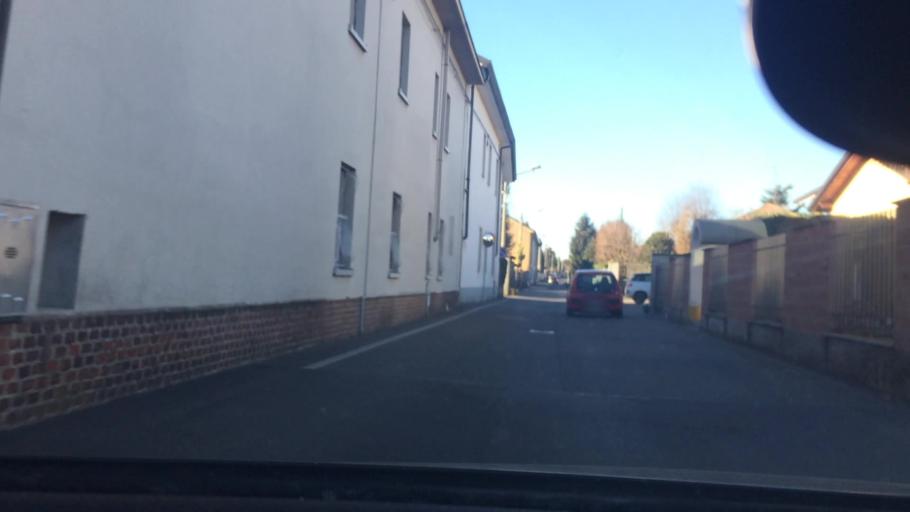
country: IT
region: Lombardy
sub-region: Provincia di Monza e Brianza
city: Ceriano Laghetto
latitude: 45.6263
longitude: 9.0790
